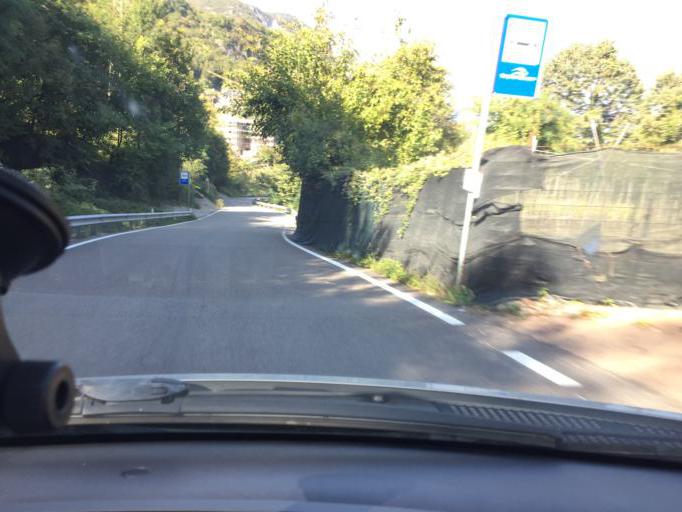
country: IT
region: Trentino-Alto Adige
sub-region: Provincia di Trento
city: Trento
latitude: 46.0717
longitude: 11.0998
